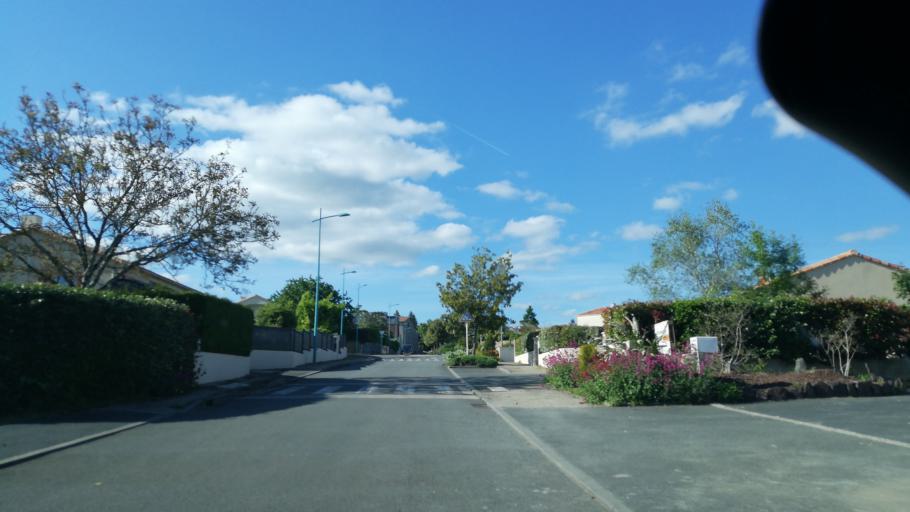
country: FR
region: Poitou-Charentes
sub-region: Departement des Deux-Sevres
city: Moncoutant
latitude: 46.7159
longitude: -0.5877
